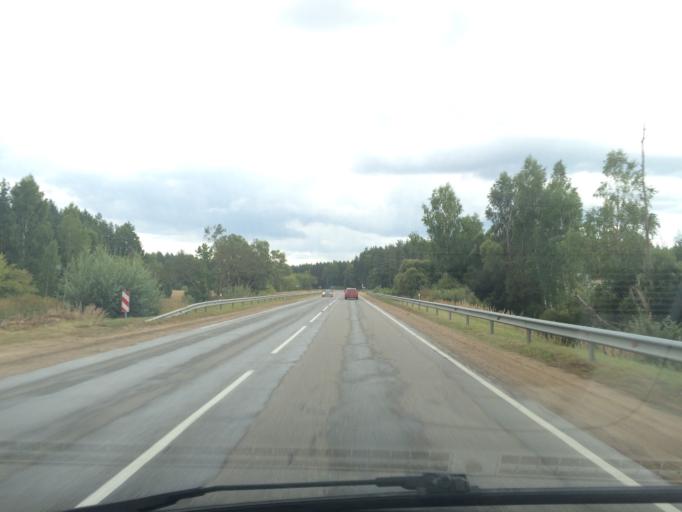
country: LV
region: Koknese
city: Koknese
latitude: 56.6021
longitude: 25.5163
